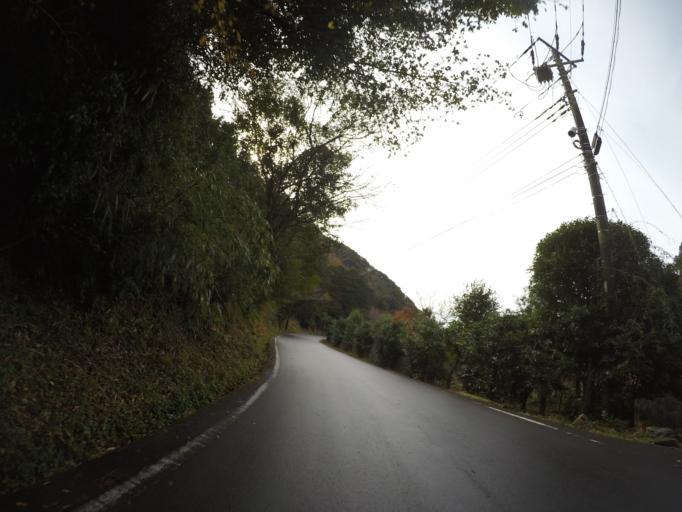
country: JP
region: Shizuoka
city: Heda
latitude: 34.8517
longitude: 138.8016
